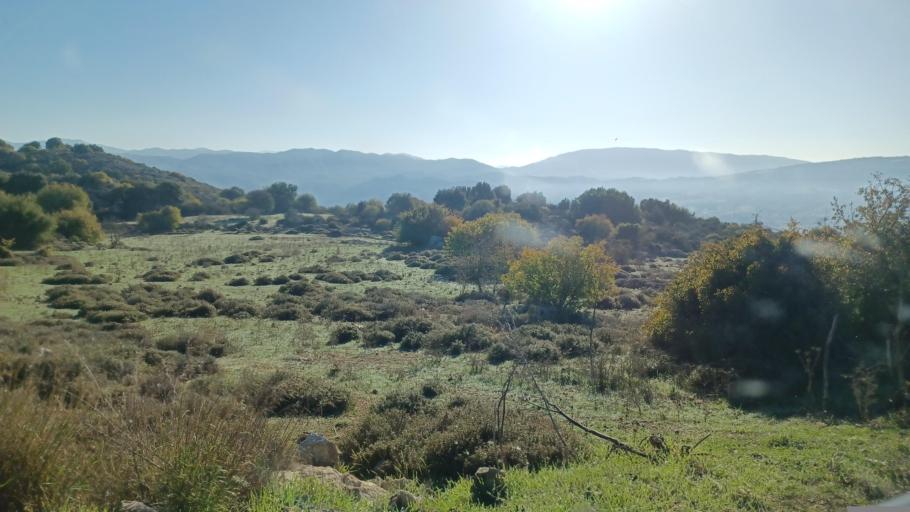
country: CY
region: Pafos
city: Polis
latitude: 34.9844
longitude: 32.5124
